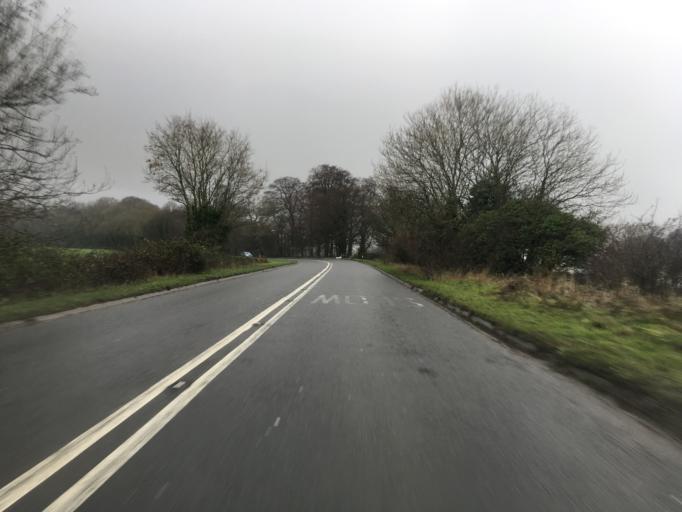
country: GB
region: England
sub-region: South Gloucestershire
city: Horton
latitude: 51.5257
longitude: -2.3433
